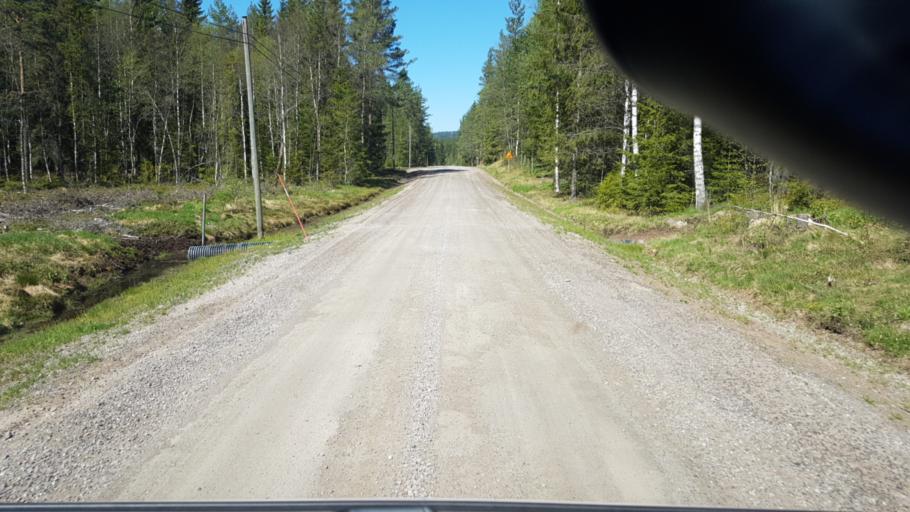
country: SE
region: Vaermland
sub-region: Eda Kommun
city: Charlottenberg
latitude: 59.9644
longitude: 12.5064
